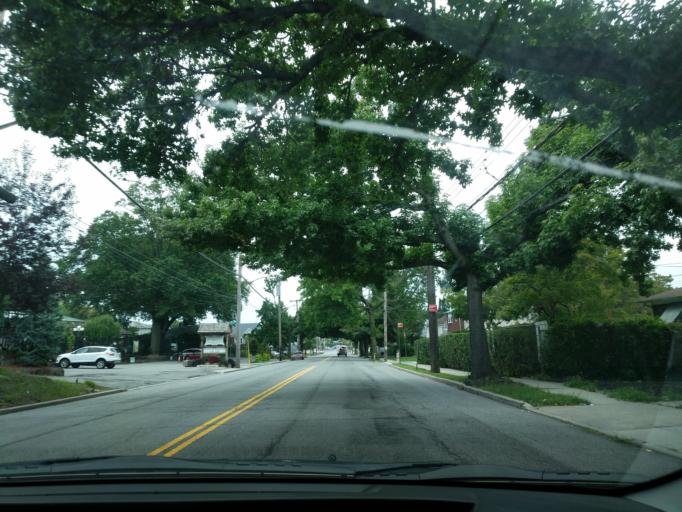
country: US
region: New York
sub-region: Richmond County
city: Bloomfield
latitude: 40.6109
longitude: -74.1434
